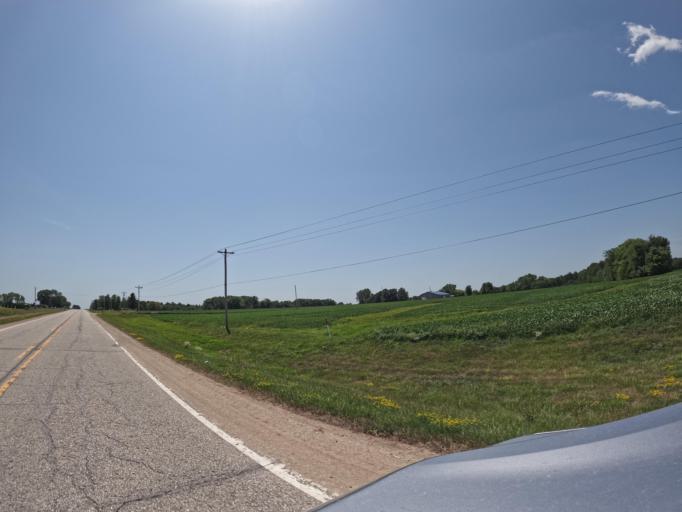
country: US
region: Iowa
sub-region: Henry County
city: Mount Pleasant
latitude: 40.9633
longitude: -91.6124
